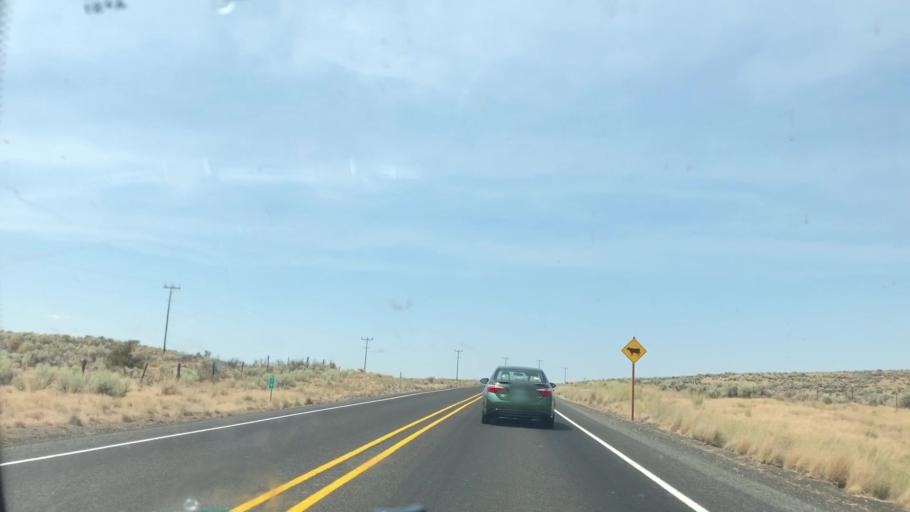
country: US
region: Idaho
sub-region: Owyhee County
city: Murphy
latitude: 42.9933
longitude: -117.0597
